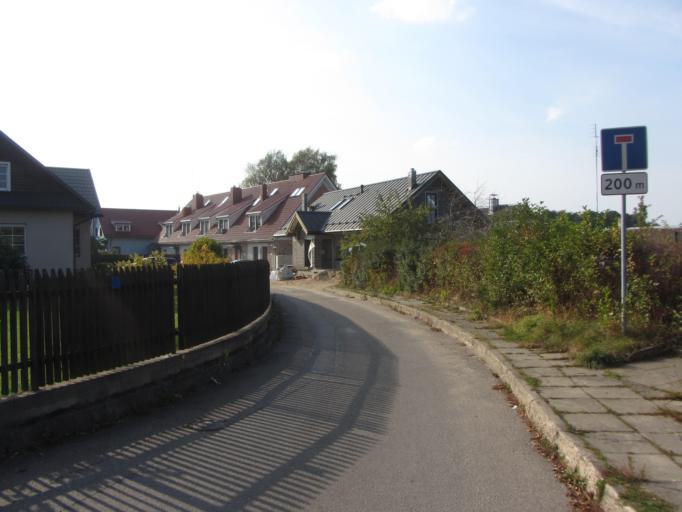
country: LT
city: Trakai
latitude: 54.6430
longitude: 24.9305
